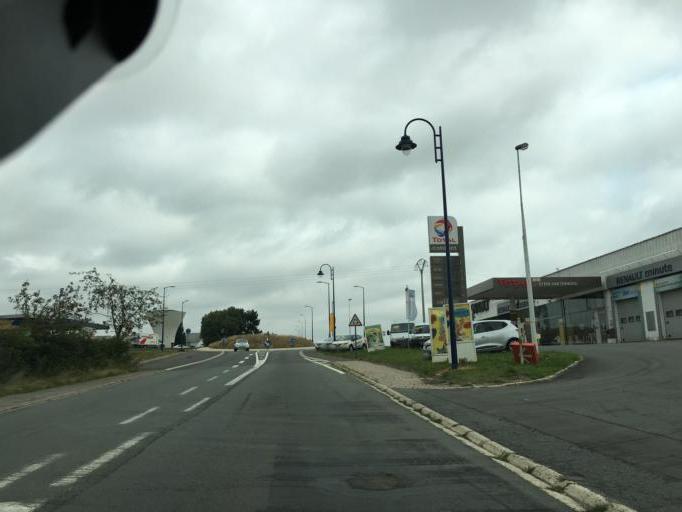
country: FR
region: Nord-Pas-de-Calais
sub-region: Departement du Pas-de-Calais
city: Saint-Pol-sur-Ternoise
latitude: 50.3868
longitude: 2.3492
